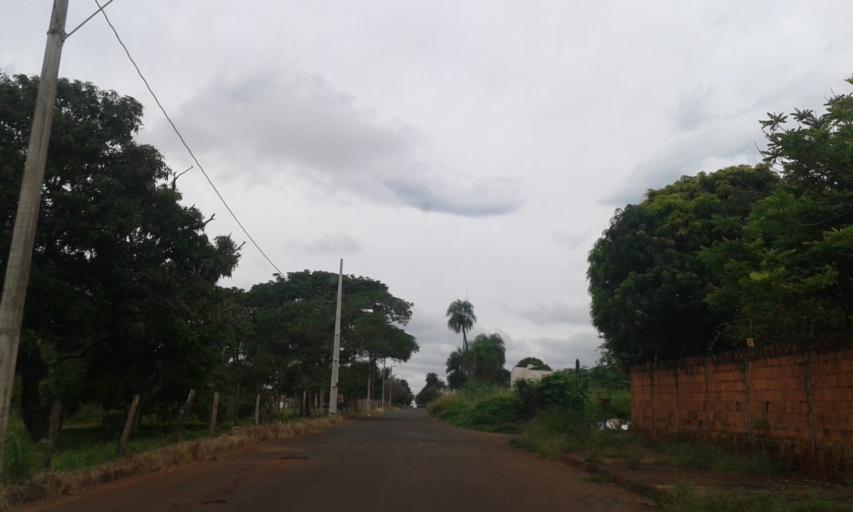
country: BR
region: Minas Gerais
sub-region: Ituiutaba
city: Ituiutaba
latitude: -18.9819
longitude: -49.4457
